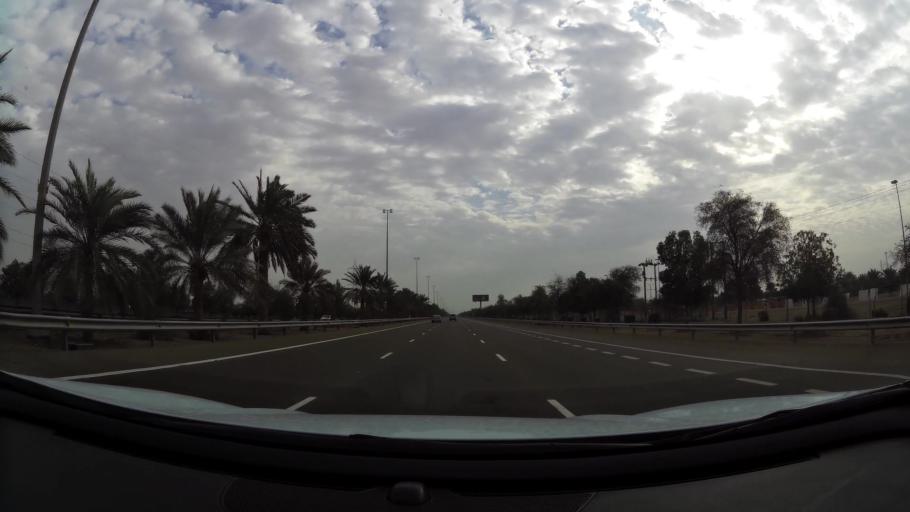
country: AE
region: Abu Dhabi
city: Al Ain
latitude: 24.2054
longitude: 55.4276
